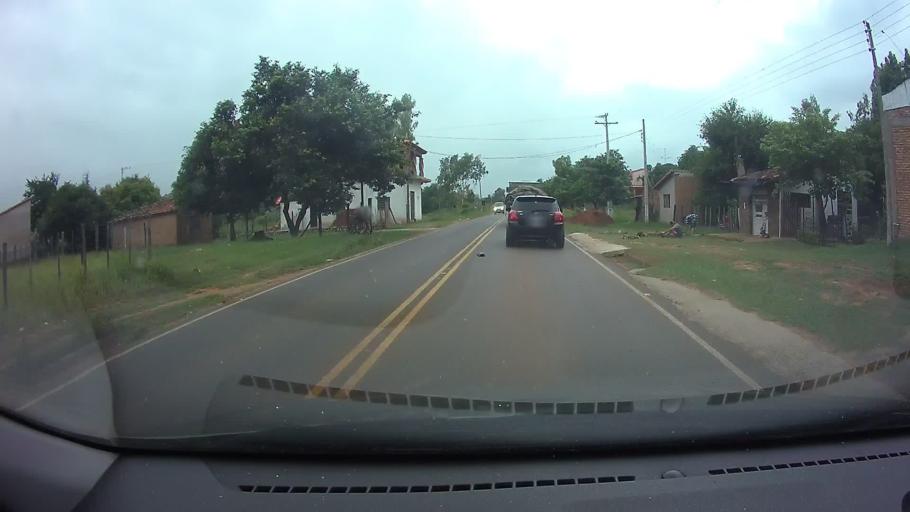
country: PY
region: Paraguari
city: Carapegua
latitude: -25.7582
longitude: -57.2547
